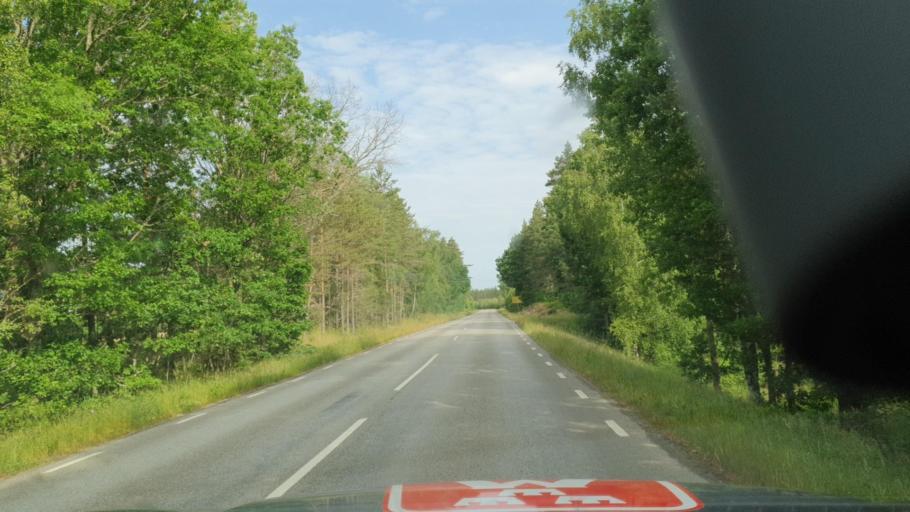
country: SE
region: Kalmar
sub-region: Kalmar Kommun
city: Trekanten
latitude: 56.6617
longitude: 16.0044
